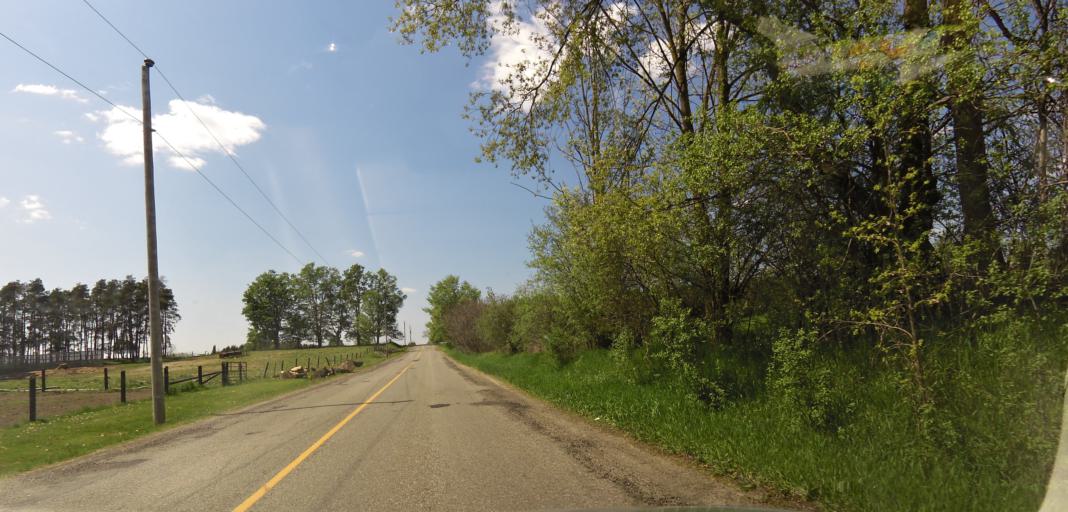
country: CA
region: Ontario
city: Brampton
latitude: 43.8412
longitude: -79.8744
